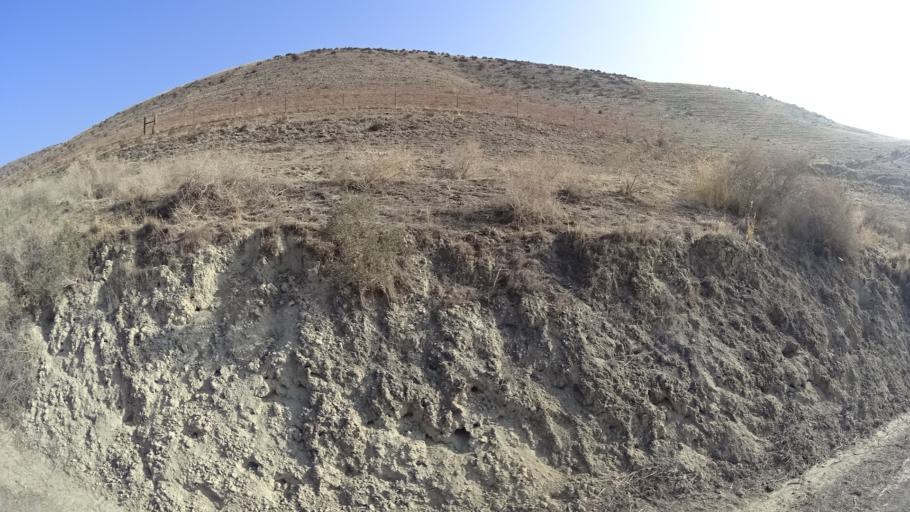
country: US
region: California
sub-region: Kern County
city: Oildale
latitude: 35.4474
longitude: -118.8283
